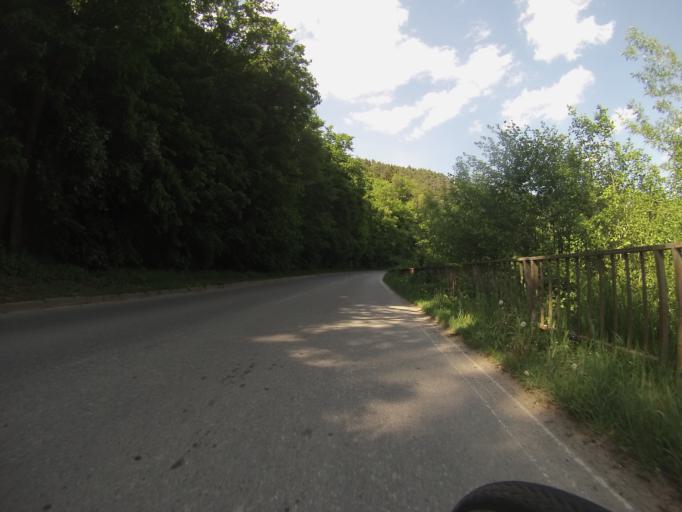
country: CZ
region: South Moravian
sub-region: Okres Blansko
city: Blansko
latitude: 49.3517
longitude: 16.6611
